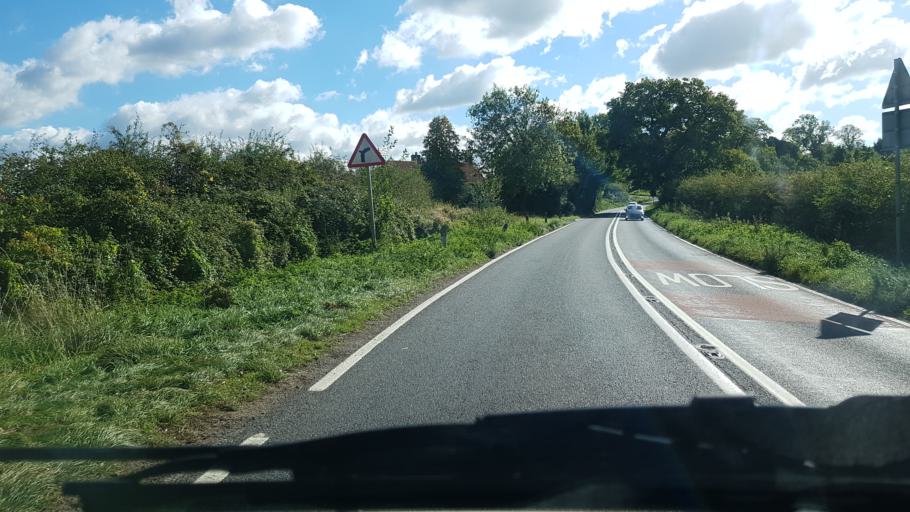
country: GB
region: England
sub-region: West Sussex
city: Billingshurst
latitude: 51.0226
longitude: -0.4755
